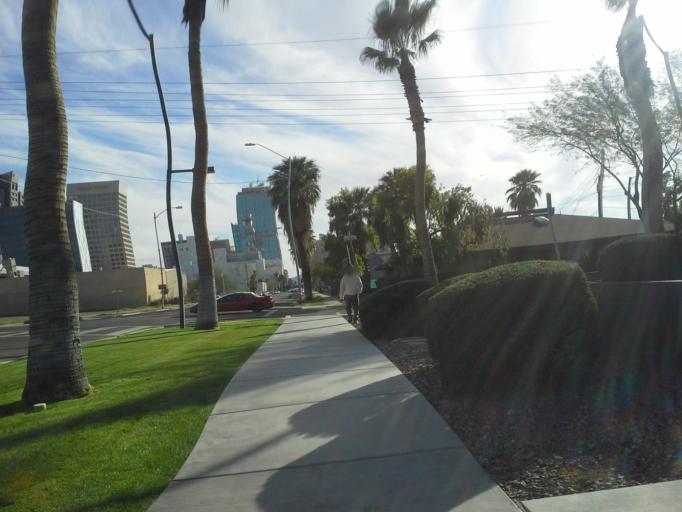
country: US
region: Arizona
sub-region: Maricopa County
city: Phoenix
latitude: 33.4551
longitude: -112.0779
